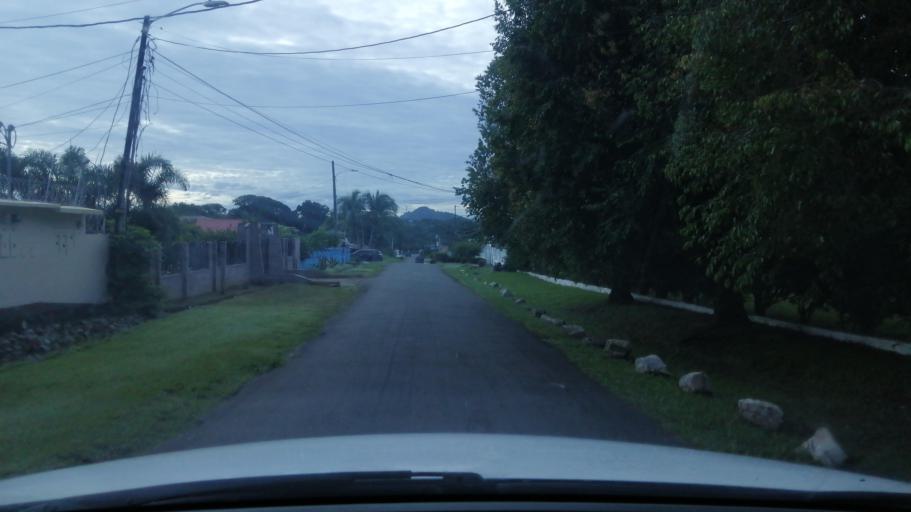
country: PA
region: Chiriqui
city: Mata del Nance
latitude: 8.4574
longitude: -82.4176
